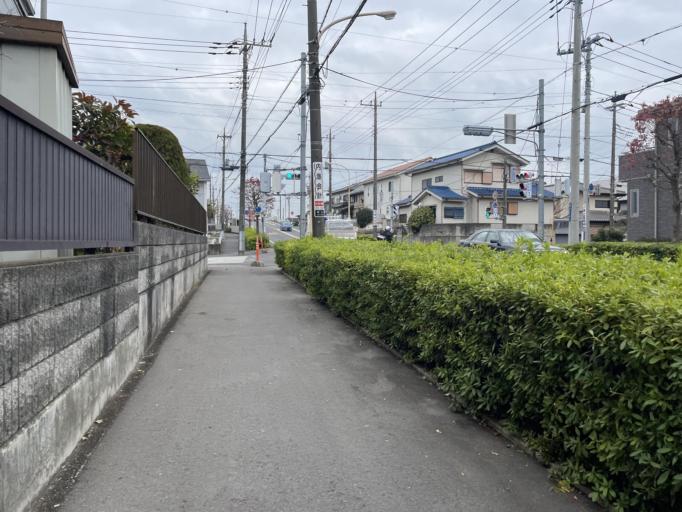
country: JP
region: Saitama
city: Shiraoka
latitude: 35.9961
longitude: 139.6599
